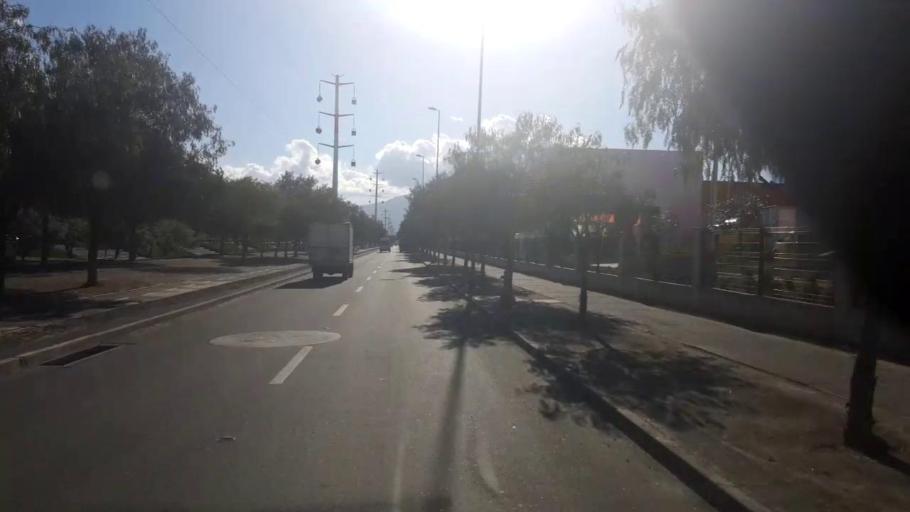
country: CL
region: Santiago Metropolitan
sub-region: Provincia de Santiago
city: Lo Prado
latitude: -33.4319
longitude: -70.7893
